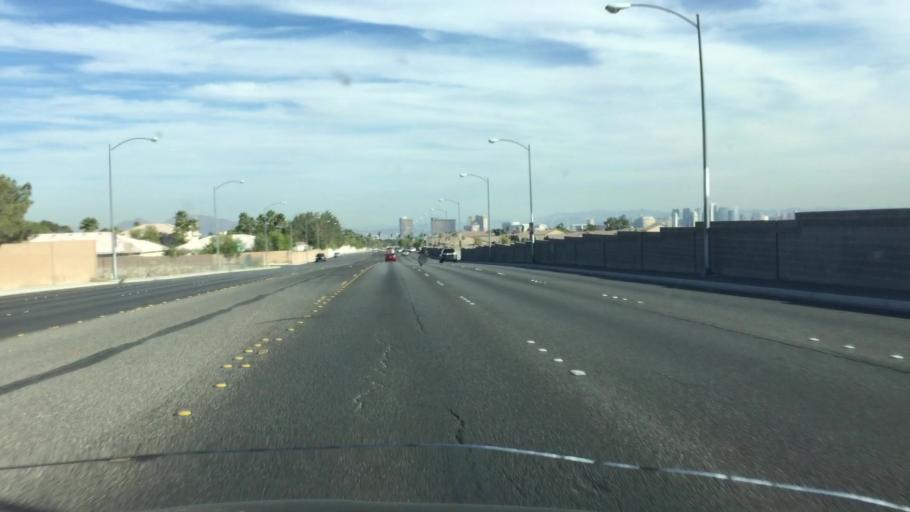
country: US
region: Nevada
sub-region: Clark County
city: Spring Valley
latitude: 36.1292
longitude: -115.2559
